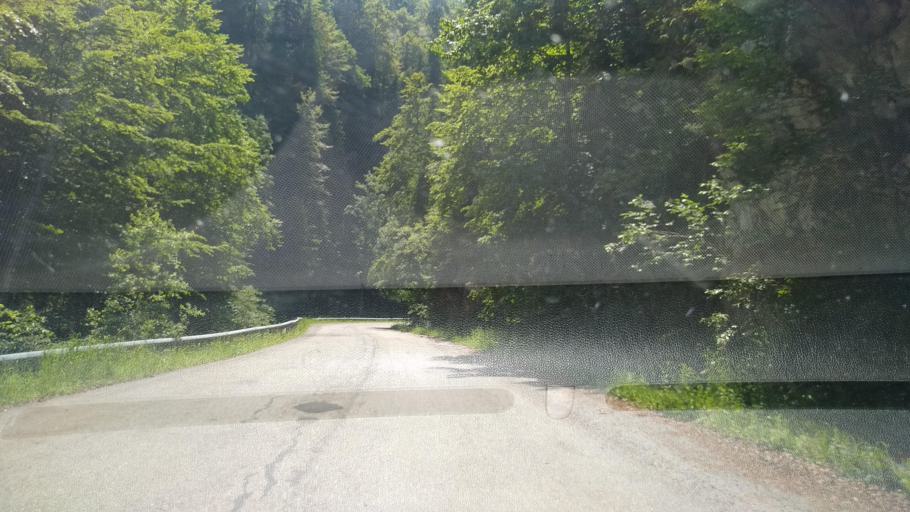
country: RO
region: Hunedoara
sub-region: Comuna Rau de Mori
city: Rau de Mori
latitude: 45.2788
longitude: 22.9147
